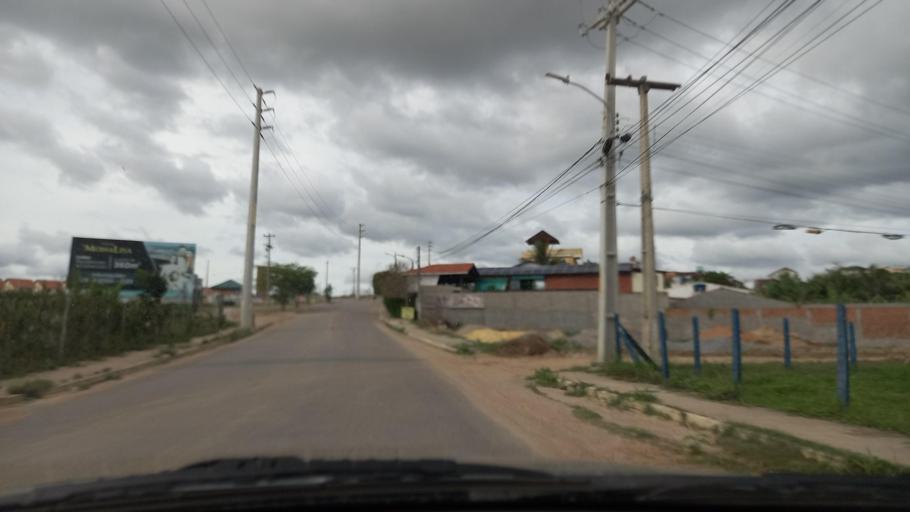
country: BR
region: Pernambuco
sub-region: Gravata
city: Gravata
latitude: -8.2034
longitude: -35.5518
